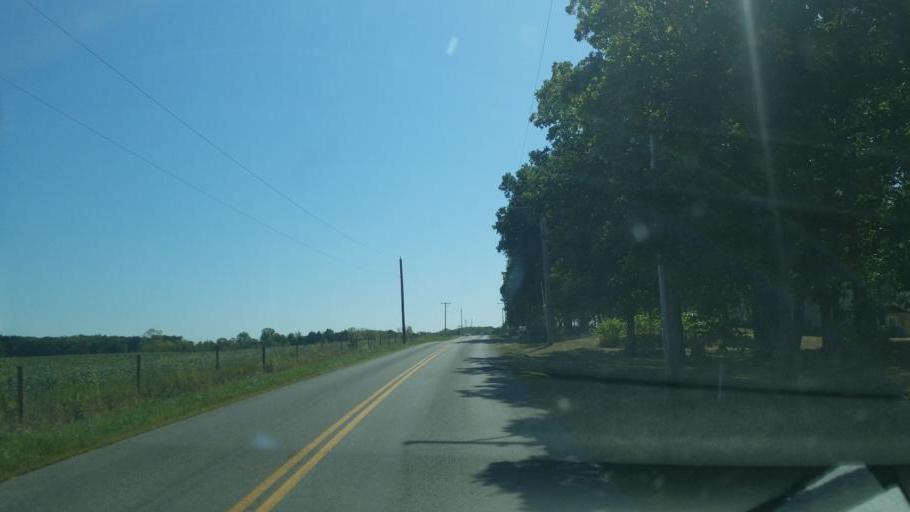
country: US
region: Ohio
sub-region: Logan County
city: Northwood
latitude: 40.4512
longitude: -83.7901
